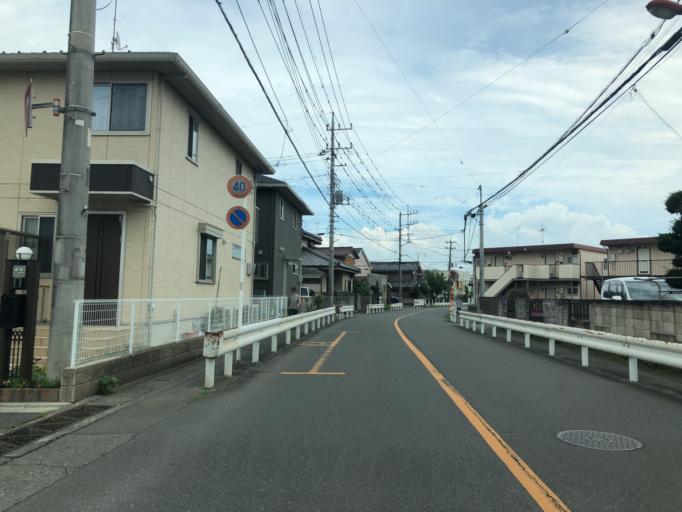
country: JP
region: Saitama
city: Fukiage-fujimi
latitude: 36.0461
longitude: 139.3940
